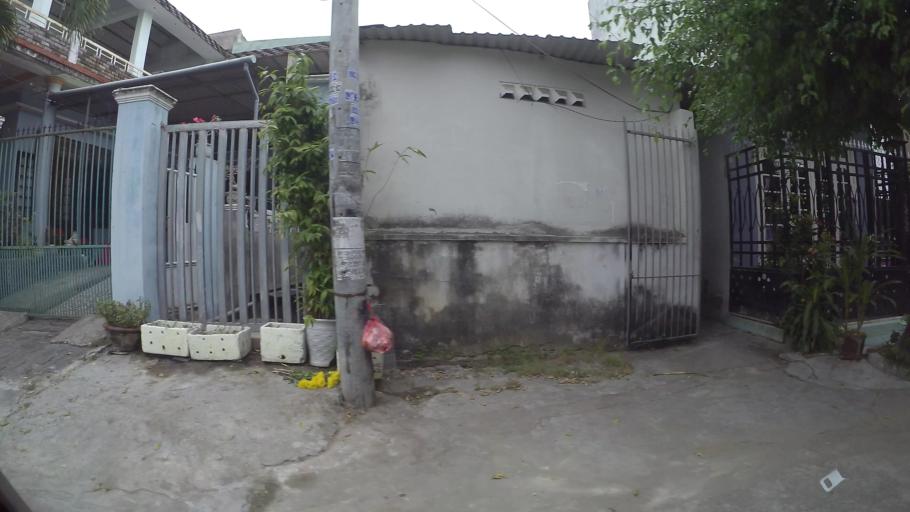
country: VN
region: Da Nang
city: Thanh Khe
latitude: 16.0680
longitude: 108.1867
